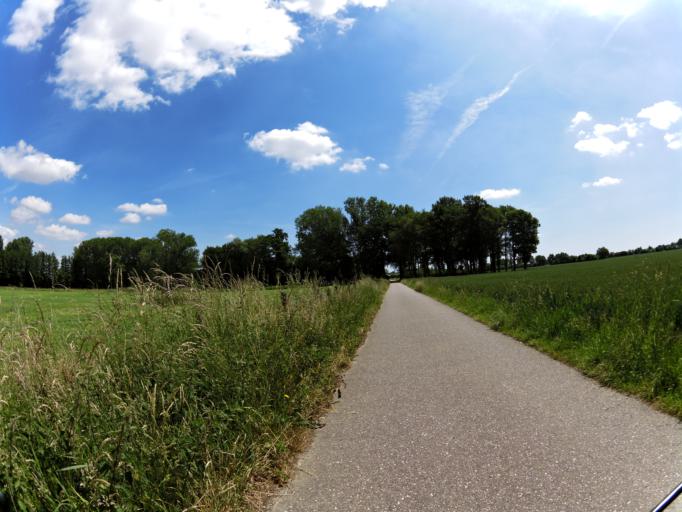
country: DE
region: North Rhine-Westphalia
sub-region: Regierungsbezirk Koln
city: Selfkant
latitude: 51.0284
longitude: 5.9208
